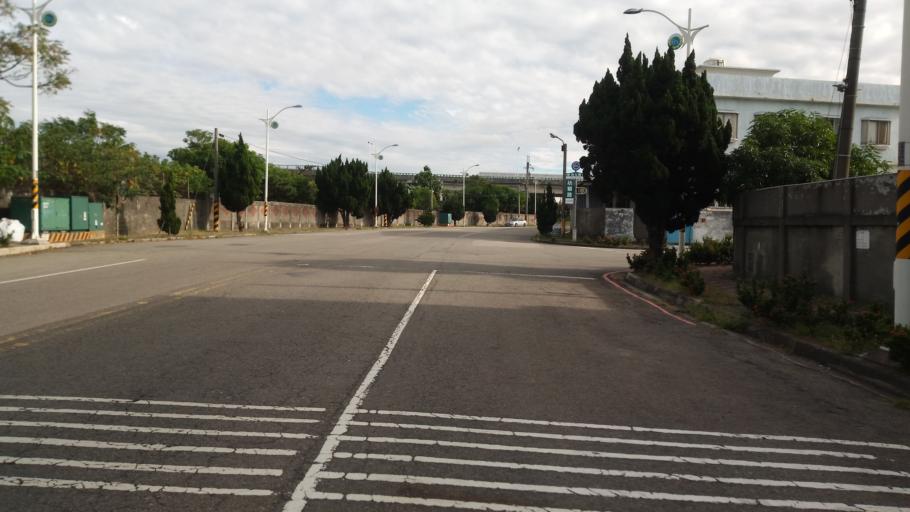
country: TW
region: Taiwan
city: Fengyuan
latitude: 24.3995
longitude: 120.6586
